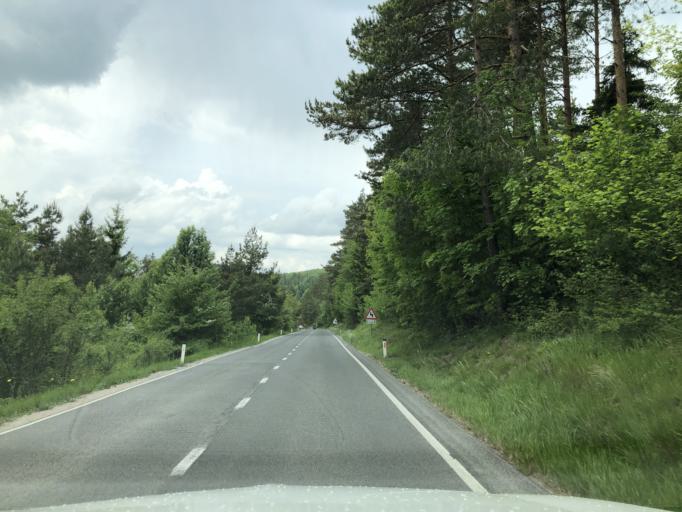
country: SI
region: Bloke
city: Nova Vas
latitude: 45.7615
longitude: 14.4600
